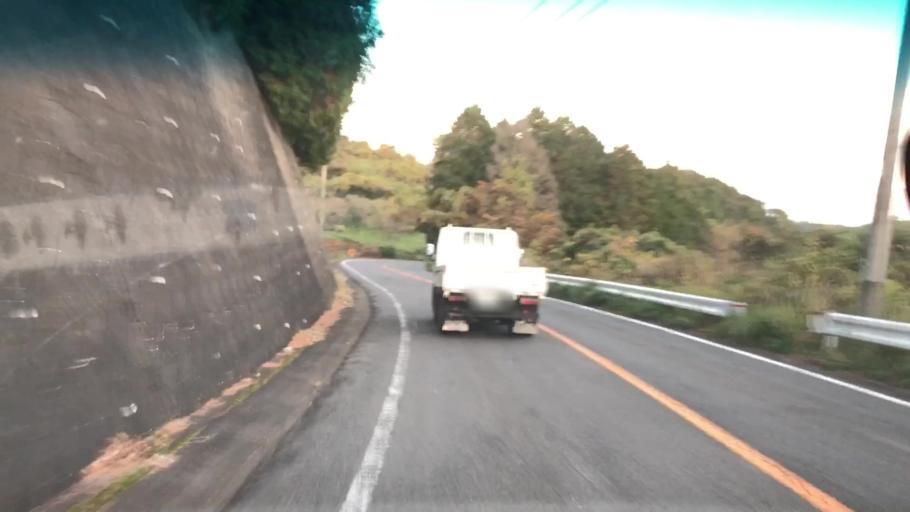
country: JP
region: Nagasaki
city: Sasebo
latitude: 33.0474
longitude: 129.7142
